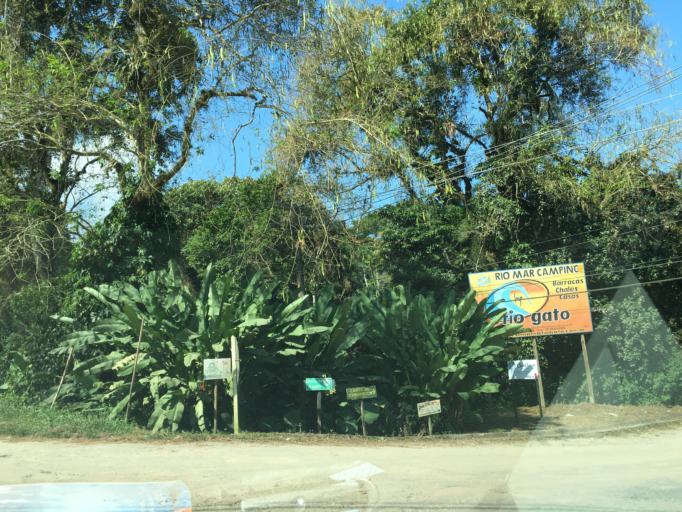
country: BR
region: Sao Paulo
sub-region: Ubatuba
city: Ubatuba
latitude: -23.3956
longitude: -45.0149
